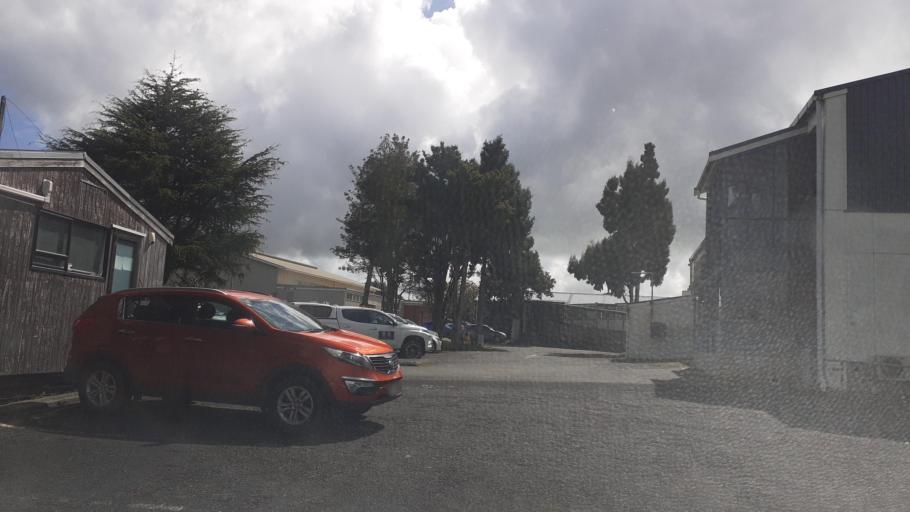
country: NZ
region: Northland
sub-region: Far North District
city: Waimate North
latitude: -35.4106
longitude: 173.8020
